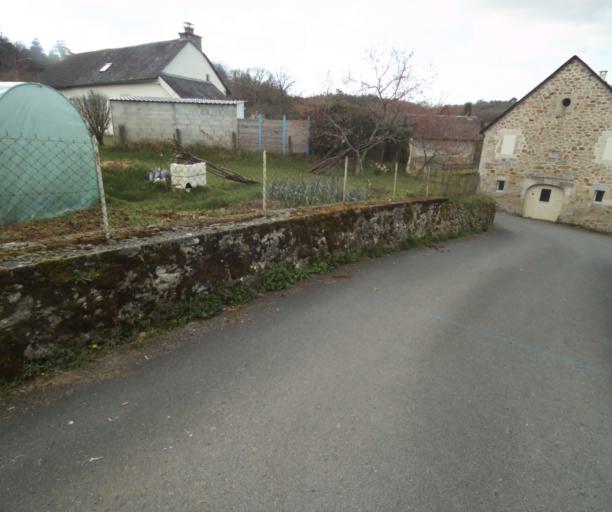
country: FR
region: Limousin
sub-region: Departement de la Correze
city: Laguenne
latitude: 45.2288
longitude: 1.8982
